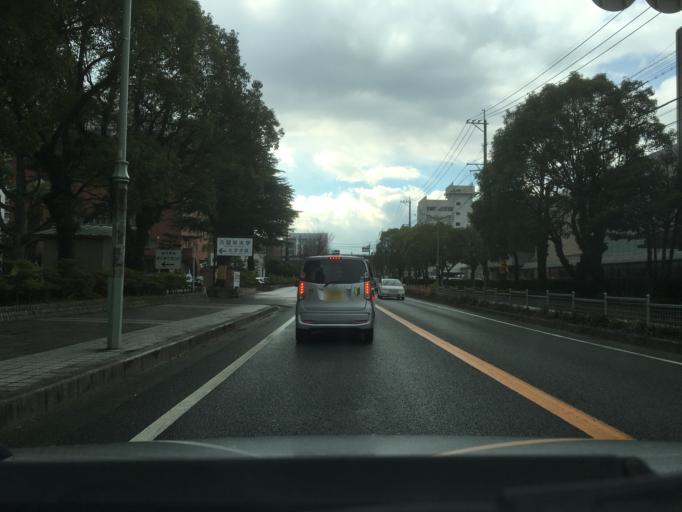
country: JP
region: Fukuoka
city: Kurume
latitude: 33.3293
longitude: 130.5108
